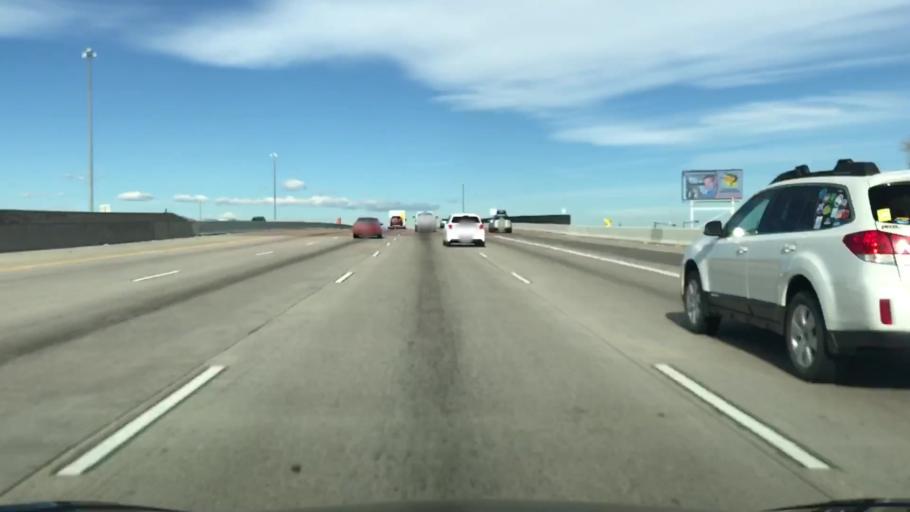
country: US
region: Colorado
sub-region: Denver County
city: Denver
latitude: 39.7009
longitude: -104.9866
